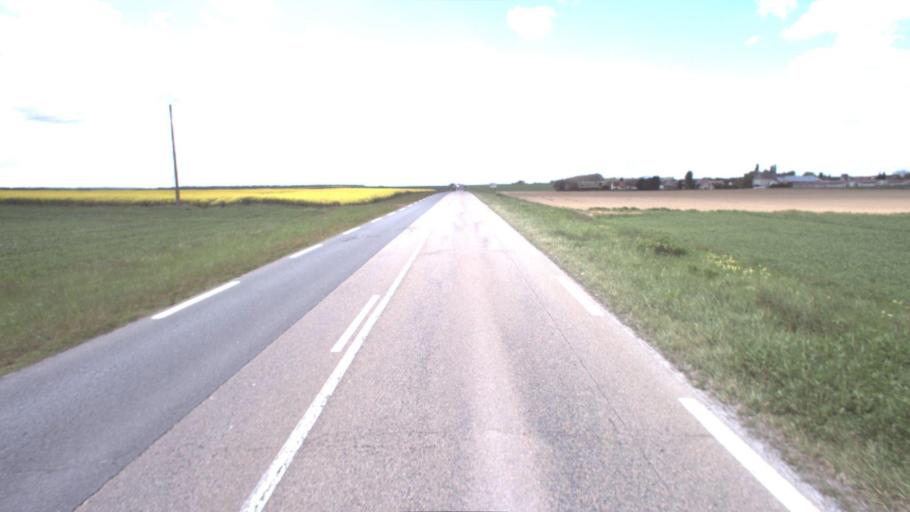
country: FR
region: Ile-de-France
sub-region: Departement de Seine-et-Marne
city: Villiers-Saint-Georges
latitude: 48.6912
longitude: 3.3516
